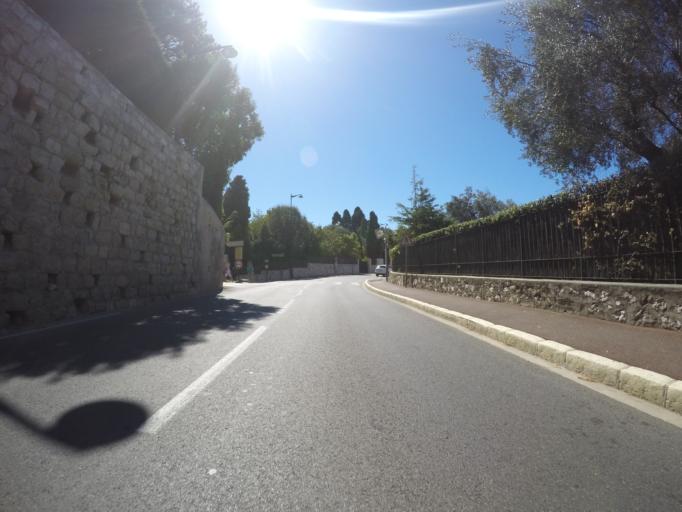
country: FR
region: Provence-Alpes-Cote d'Azur
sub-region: Departement des Alpes-Maritimes
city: Saint-Jean-Cap-Ferrat
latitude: 43.6942
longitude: 7.3286
